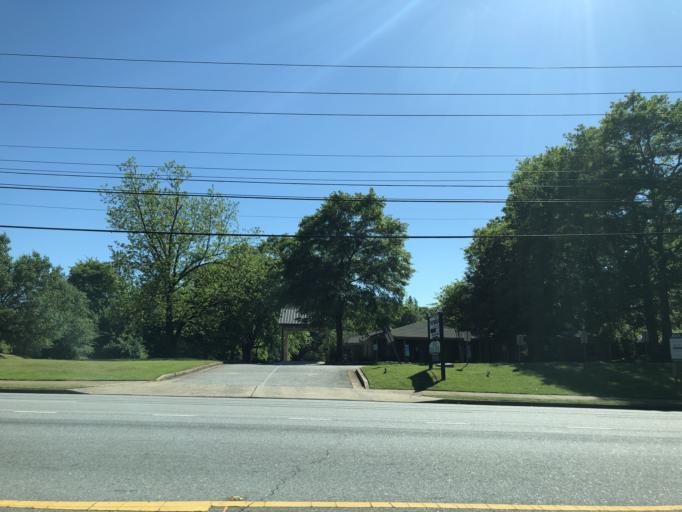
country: US
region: Georgia
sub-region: Clarke County
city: Country Club Estates
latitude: 33.9696
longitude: -83.4092
